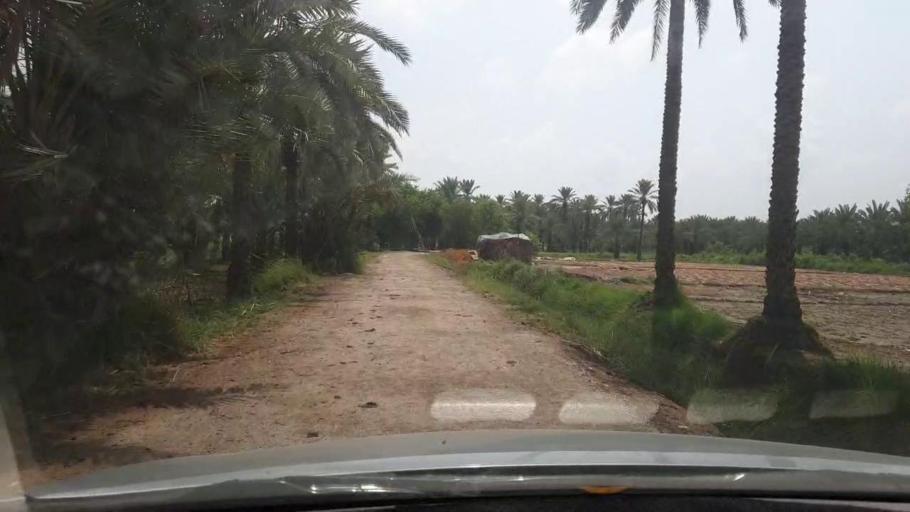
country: PK
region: Sindh
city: Khairpur
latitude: 27.5035
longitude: 68.7402
